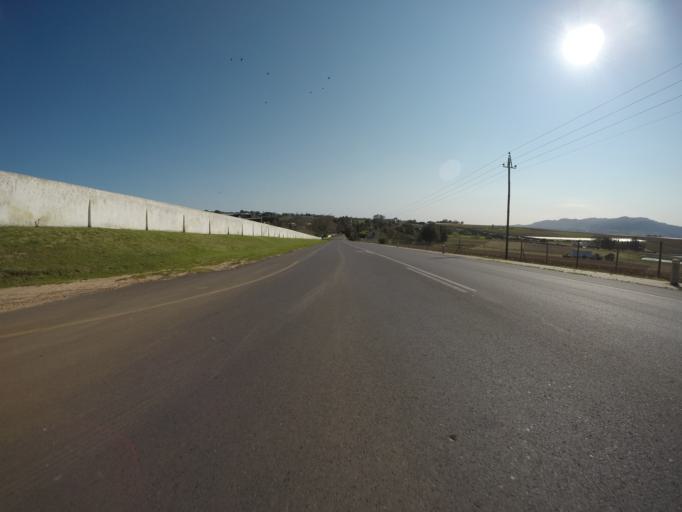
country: ZA
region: Western Cape
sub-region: Cape Winelands District Municipality
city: Noorder-Paarl
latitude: -33.6707
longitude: 18.9222
